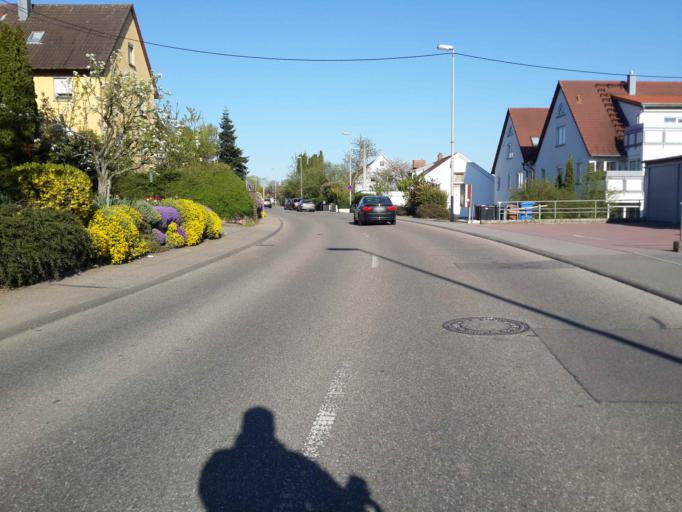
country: DE
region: Baden-Wuerttemberg
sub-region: Regierungsbezirk Stuttgart
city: Leingarten
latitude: 49.1479
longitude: 9.1115
